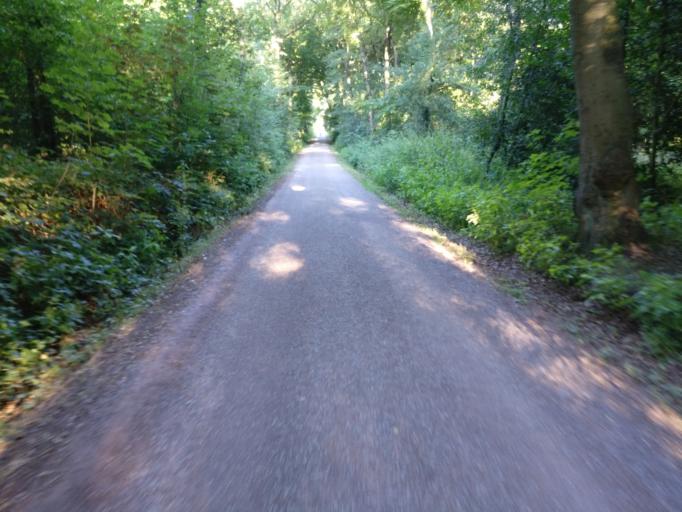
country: DE
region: North Rhine-Westphalia
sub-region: Regierungsbezirk Dusseldorf
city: Duisburg
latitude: 51.4247
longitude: 6.8019
